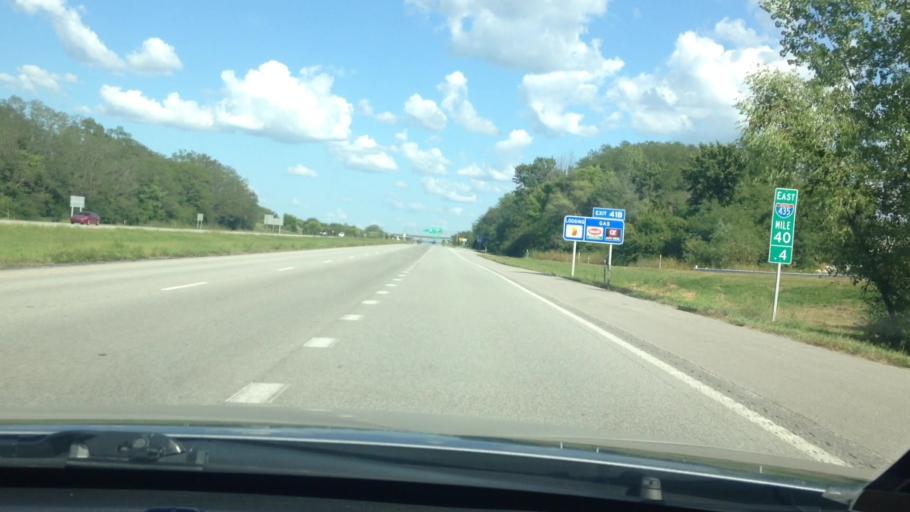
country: US
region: Missouri
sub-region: Clay County
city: Smithville
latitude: 39.3071
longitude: -94.5992
